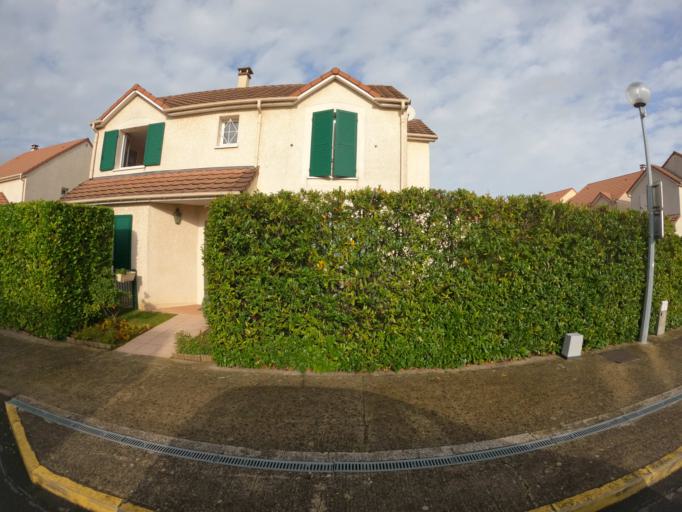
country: FR
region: Ile-de-France
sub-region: Departement de Seine-et-Marne
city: Courtry
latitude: 48.9148
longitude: 2.5965
